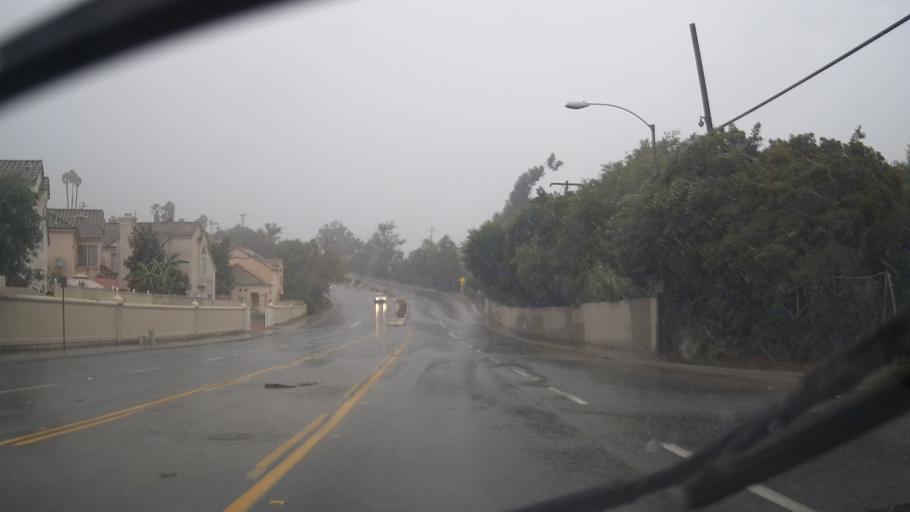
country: US
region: California
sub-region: San Diego County
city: Bonita
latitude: 32.6605
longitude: -117.0556
